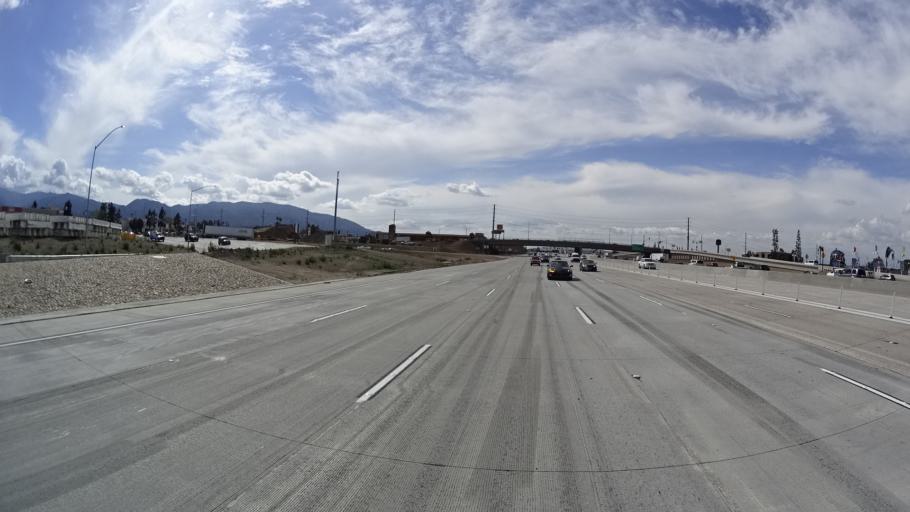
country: US
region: California
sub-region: Riverside County
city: Corona
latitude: 33.8814
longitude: -117.5801
